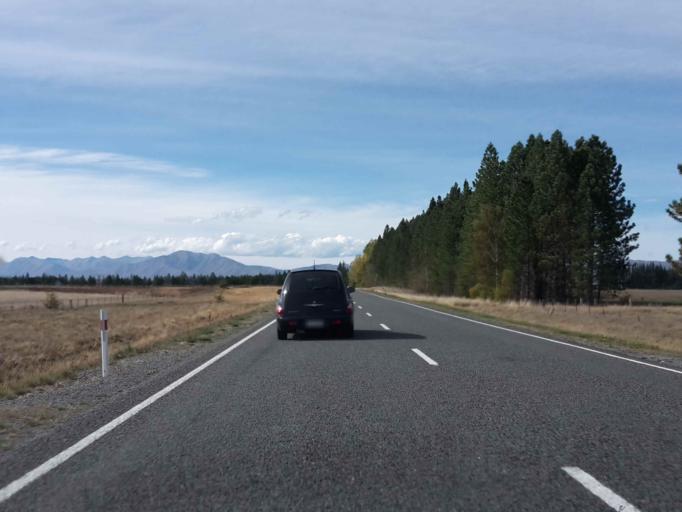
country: NZ
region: Canterbury
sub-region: Timaru District
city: Pleasant Point
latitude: -44.1894
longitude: 170.2969
